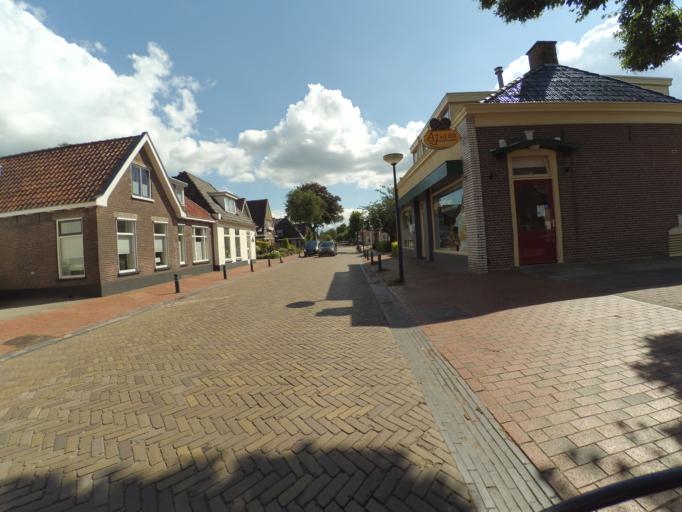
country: NL
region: Friesland
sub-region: Gemeente Achtkarspelen
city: Drogeham
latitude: 53.2025
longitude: 6.1144
